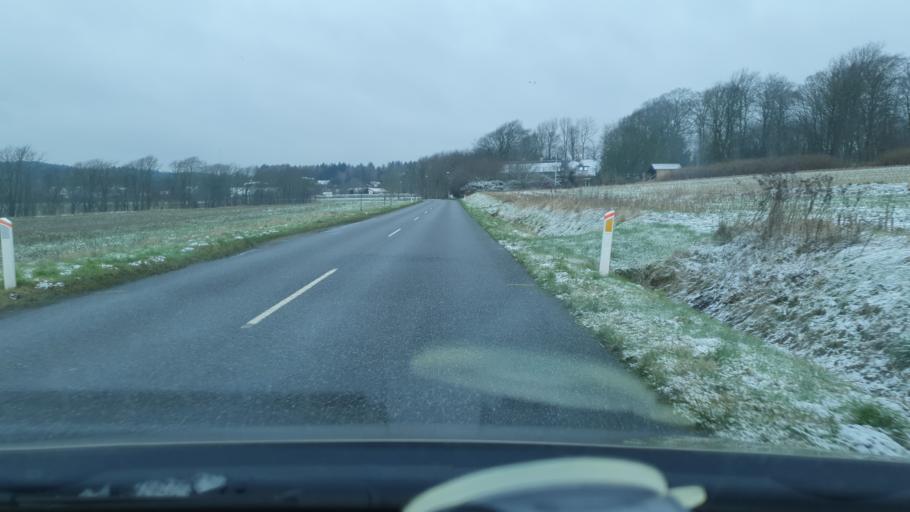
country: DK
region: North Denmark
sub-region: Jammerbugt Kommune
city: Brovst
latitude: 57.1298
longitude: 9.4721
